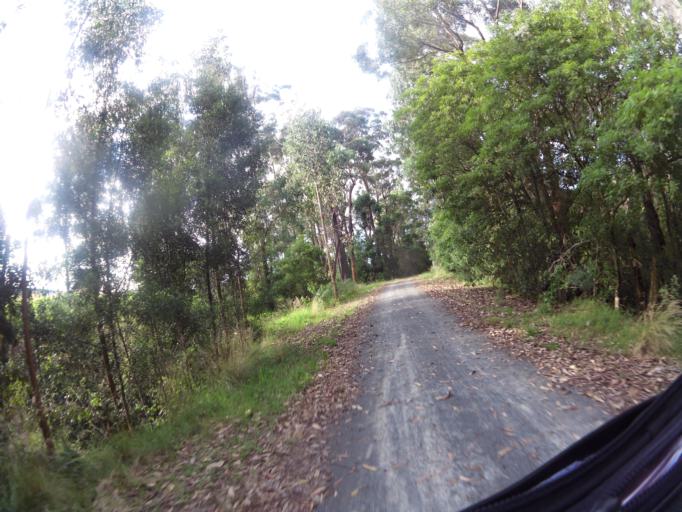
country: AU
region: Victoria
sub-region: East Gippsland
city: Lakes Entrance
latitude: -37.7335
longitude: 148.4272
